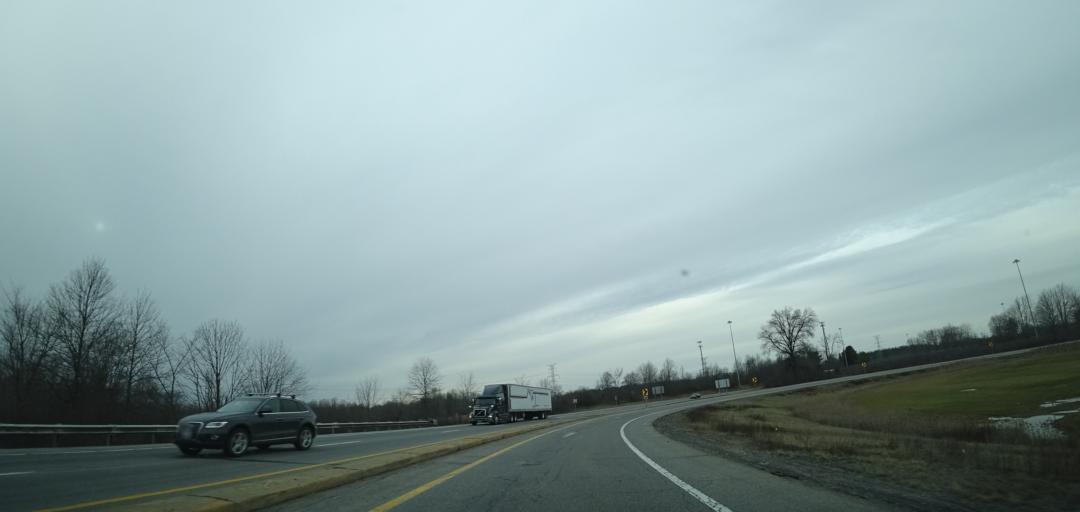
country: US
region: Ohio
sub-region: Trumbull County
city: Lordstown
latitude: 41.1141
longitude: -80.8427
